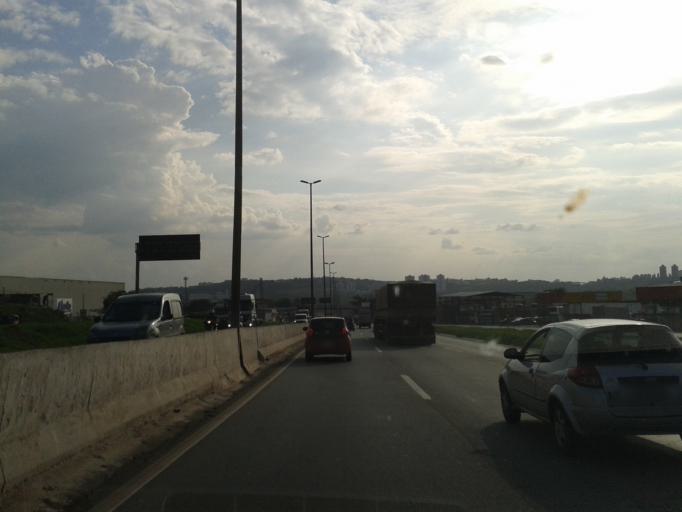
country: BR
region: Minas Gerais
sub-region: Belo Horizonte
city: Belo Horizonte
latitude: -19.8810
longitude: -43.9556
